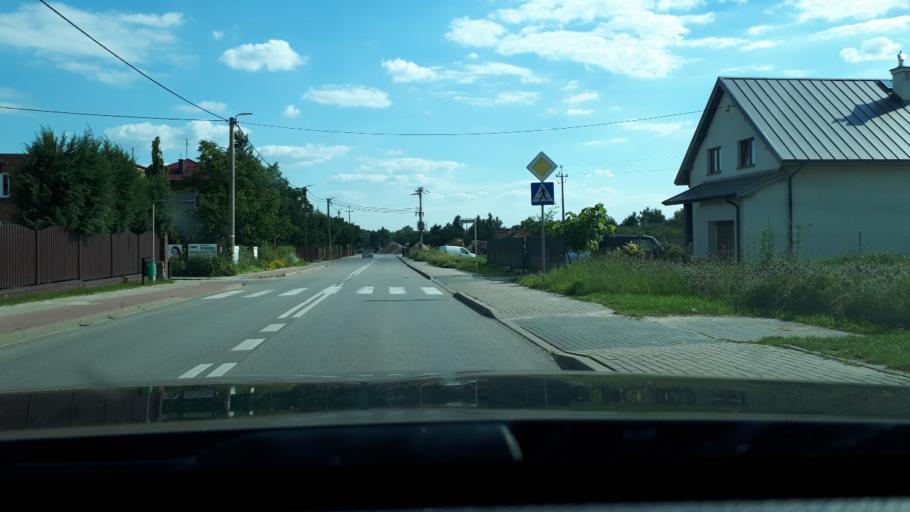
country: PL
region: Masovian Voivodeship
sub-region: Powiat grojecki
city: Warka
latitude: 51.7865
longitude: 21.1777
